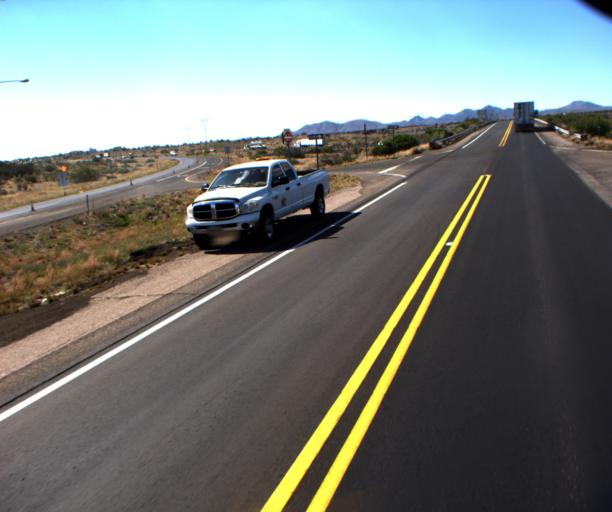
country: US
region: Arizona
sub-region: Mohave County
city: New Kingman-Butler
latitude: 35.1576
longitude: -113.6954
